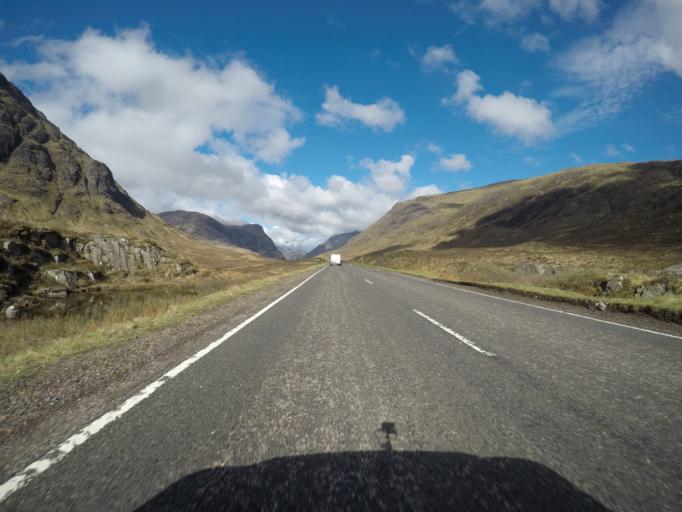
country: GB
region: Scotland
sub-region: Highland
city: Spean Bridge
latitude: 56.6628
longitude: -4.9296
